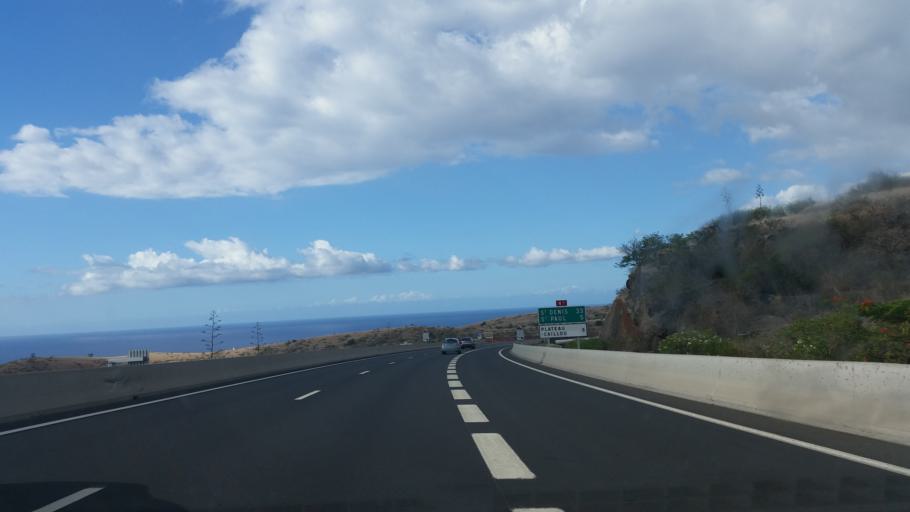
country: RE
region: Reunion
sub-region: Reunion
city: Saint-Paul
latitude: -21.0385
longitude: 55.2485
